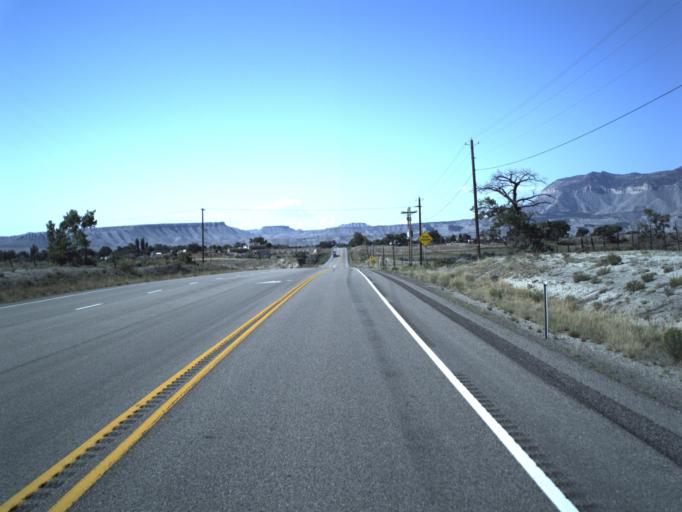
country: US
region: Utah
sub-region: Emery County
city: Ferron
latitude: 39.1089
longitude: -111.1272
